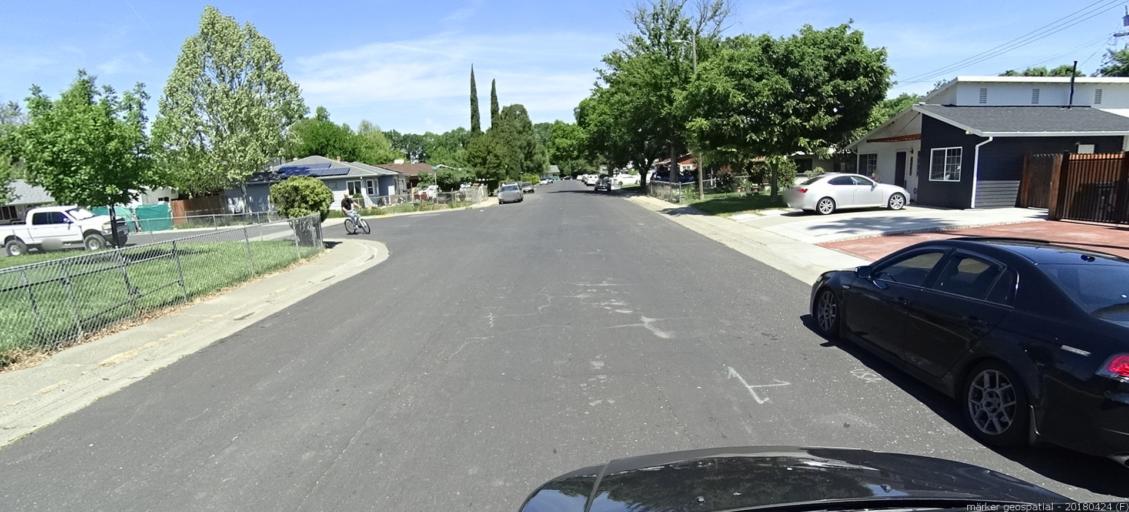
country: US
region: California
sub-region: Yolo County
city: West Sacramento
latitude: 38.5574
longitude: -121.5343
